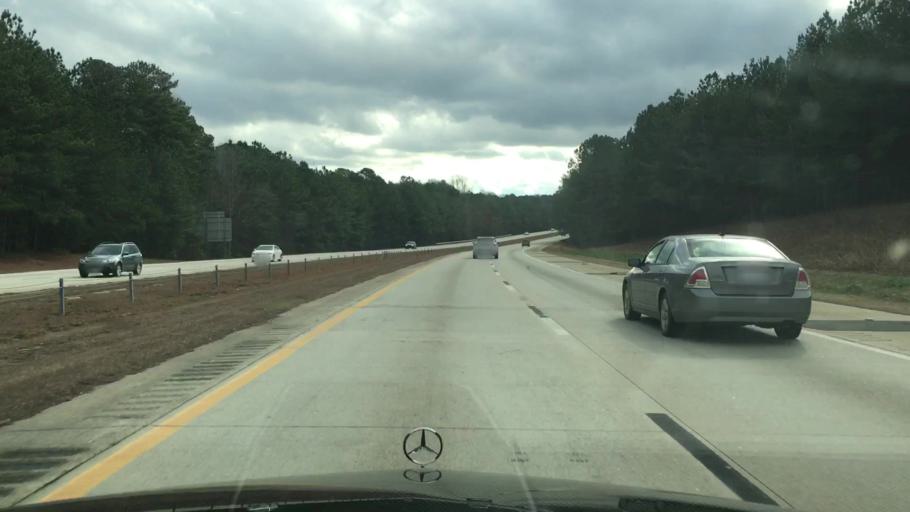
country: US
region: North Carolina
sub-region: Wake County
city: Garner
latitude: 35.6754
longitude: -78.5639
